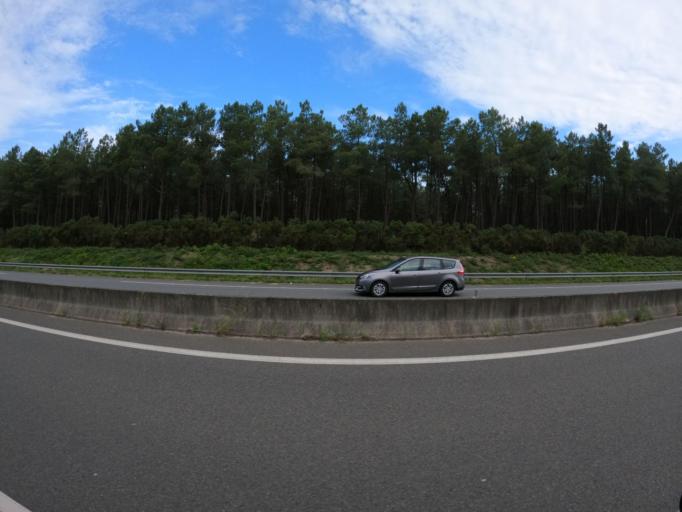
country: FR
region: Centre
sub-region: Departement d'Indre-et-Loire
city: Restigne
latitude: 47.3014
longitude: 0.2933
